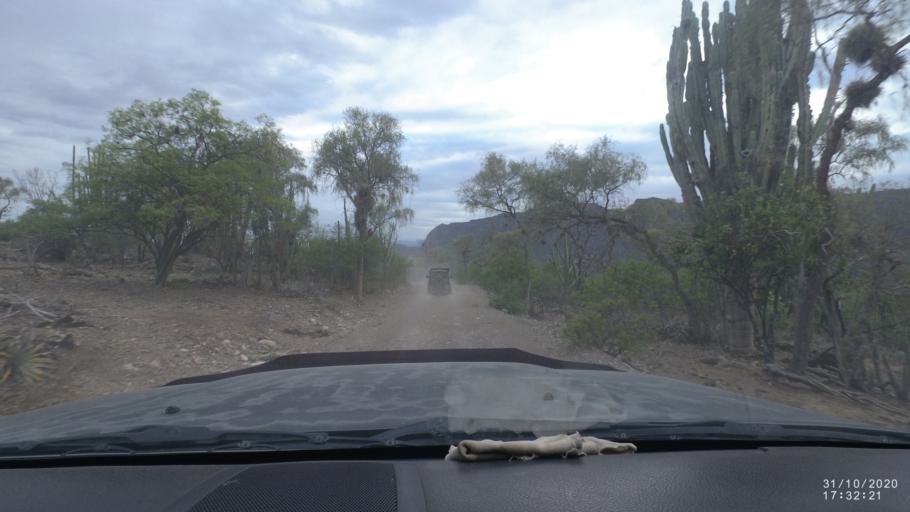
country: BO
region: Chuquisaca
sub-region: Provincia Zudanez
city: Mojocoya
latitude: -18.5986
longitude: -64.5533
